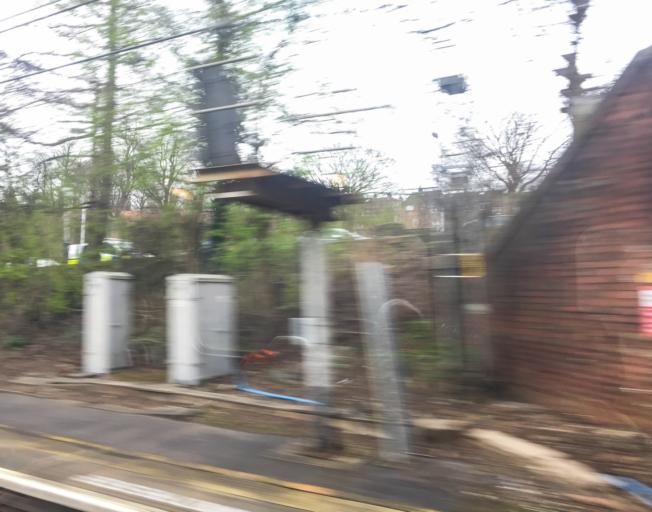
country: GB
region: Scotland
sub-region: West Dunbartonshire
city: Duntocher
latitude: 55.9114
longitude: -4.4252
